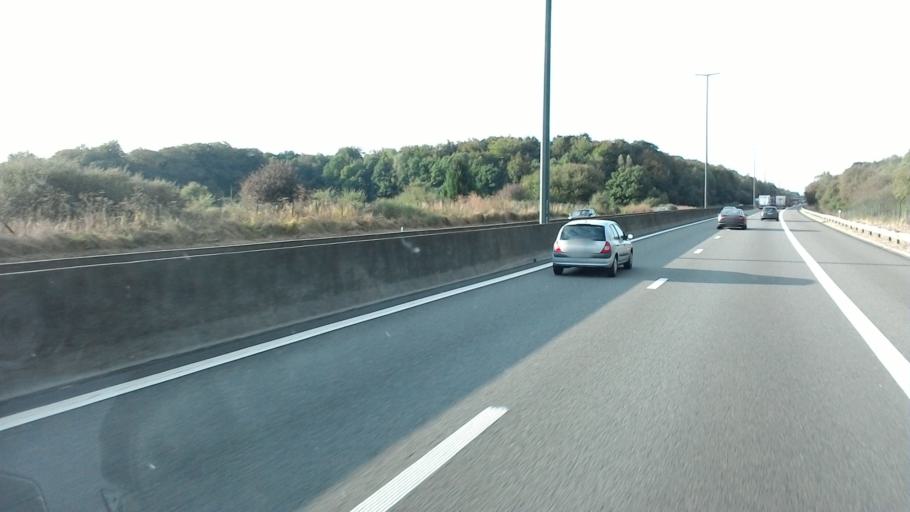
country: BE
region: Wallonia
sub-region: Province du Luxembourg
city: Habay-la-Vieille
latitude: 49.7307
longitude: 5.5803
